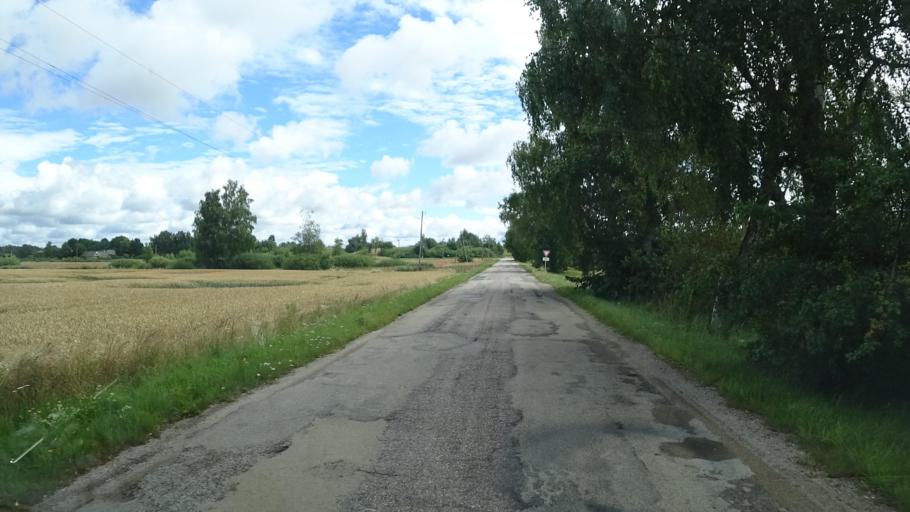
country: LV
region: Grobina
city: Grobina
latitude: 56.6577
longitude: 21.1247
